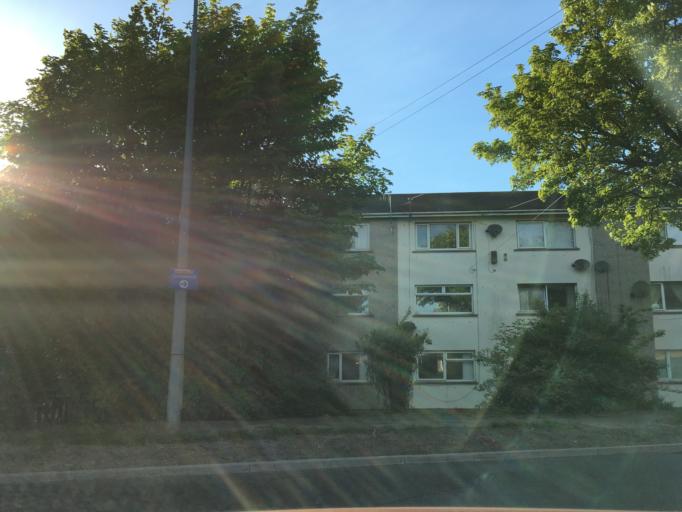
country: GB
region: Wales
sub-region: Newport
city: Marshfield
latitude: 51.5034
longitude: -3.1217
